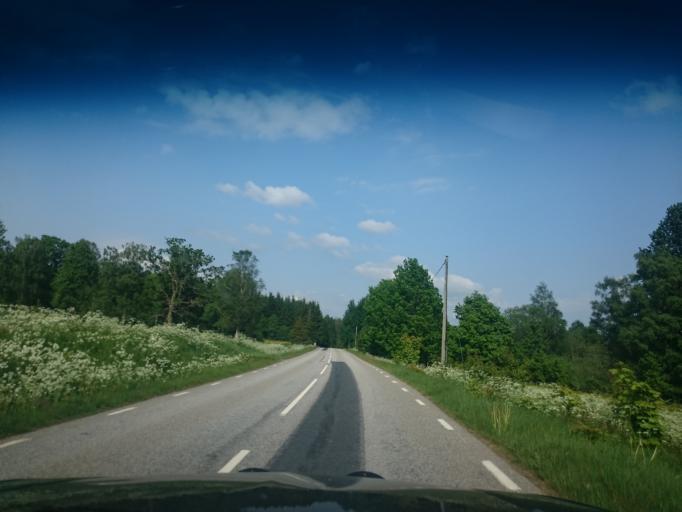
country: SE
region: Joenkoeping
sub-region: Vetlanda Kommun
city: Vetlanda
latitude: 57.3220
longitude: 15.0968
